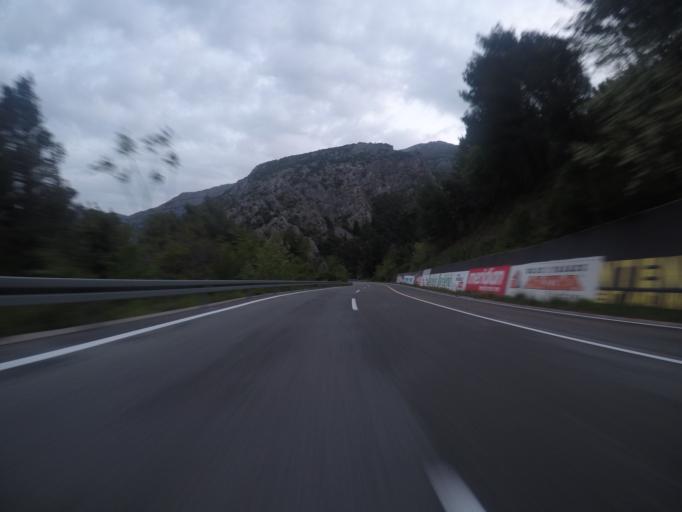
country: ME
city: Petrovac na Moru
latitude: 42.1887
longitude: 18.9887
